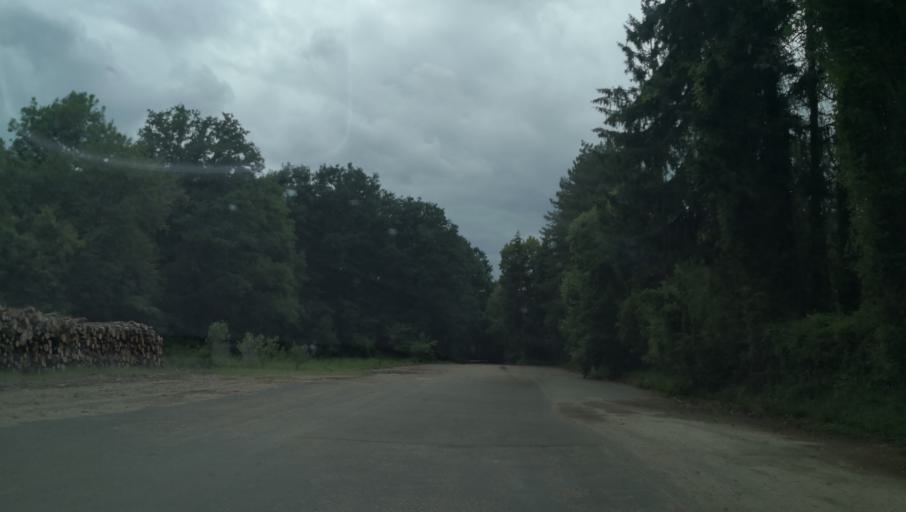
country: FR
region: Ile-de-France
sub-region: Departement des Yvelines
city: Guyancourt
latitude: 48.7815
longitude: 2.0856
